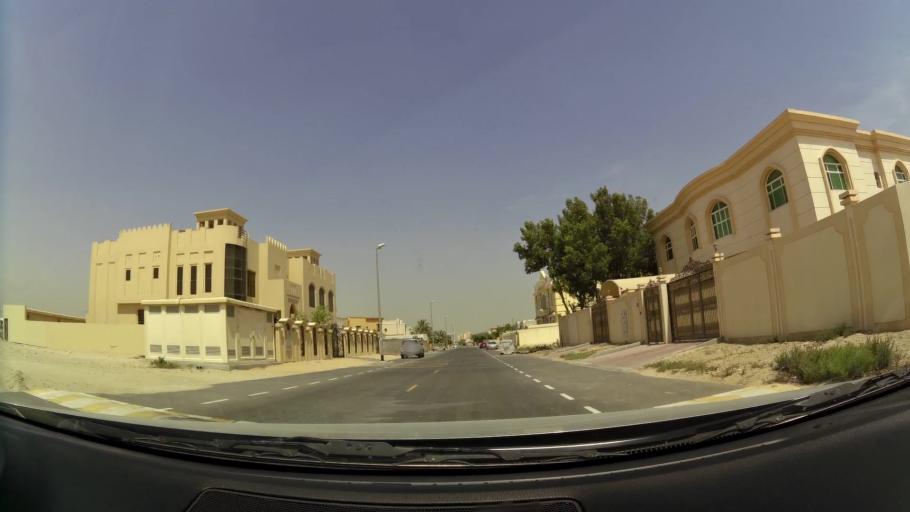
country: AE
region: Ash Shariqah
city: Sharjah
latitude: 25.1773
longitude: 55.4212
